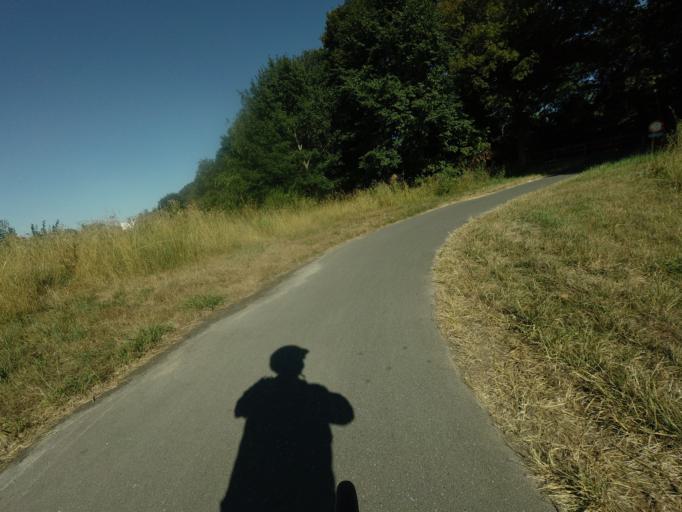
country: BE
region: Flanders
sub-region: Provincie Antwerpen
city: Turnhout
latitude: 51.3304
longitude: 4.9388
